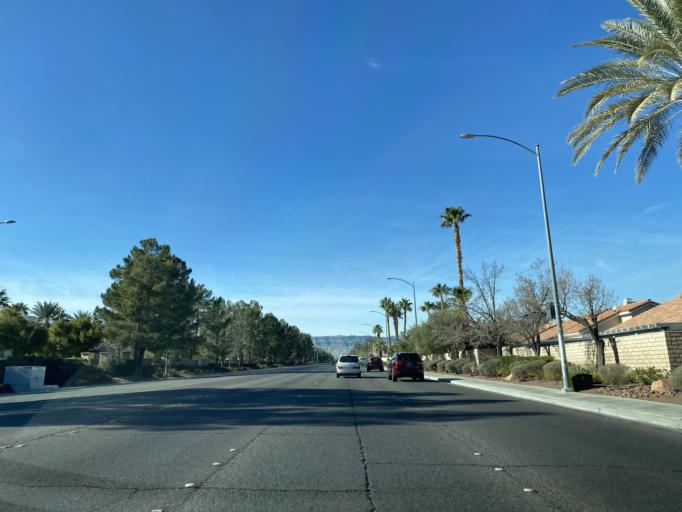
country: US
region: Nevada
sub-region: Clark County
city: Spring Valley
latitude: 36.0998
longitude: -115.2673
